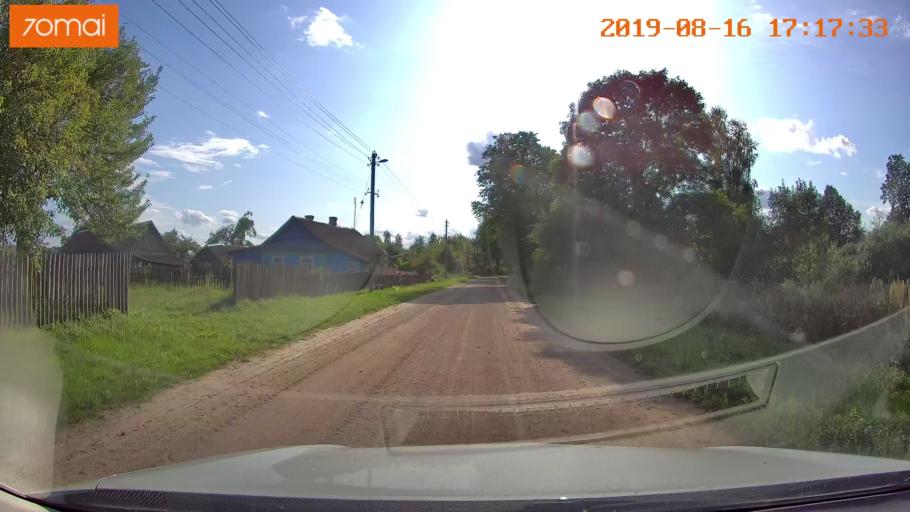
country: BY
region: Mogilev
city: Hlusha
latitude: 53.1706
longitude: 28.8059
